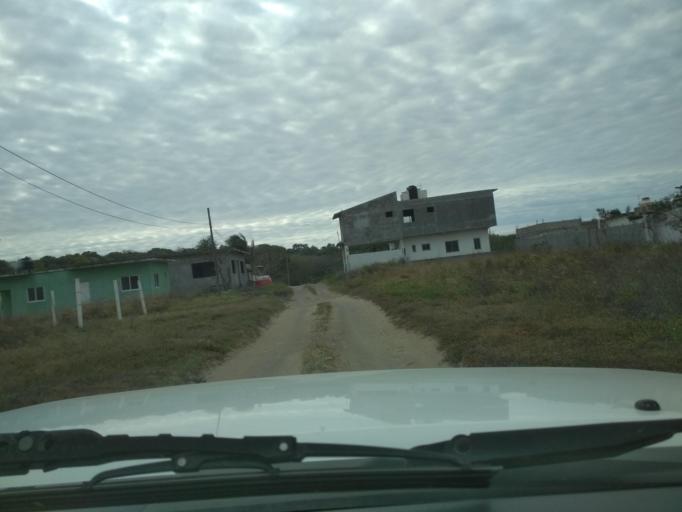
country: MX
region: Veracruz
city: Anton Lizardo
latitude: 19.0526
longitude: -95.9892
